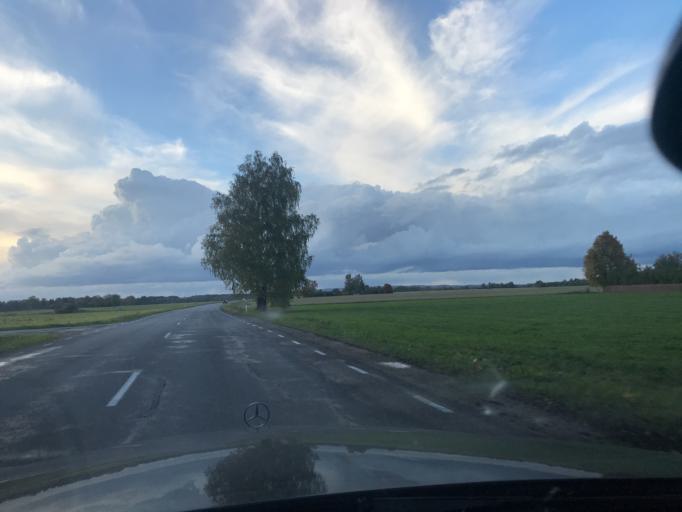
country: EE
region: Vorumaa
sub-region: Antsla vald
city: Vana-Antsla
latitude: 57.8967
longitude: 26.4851
